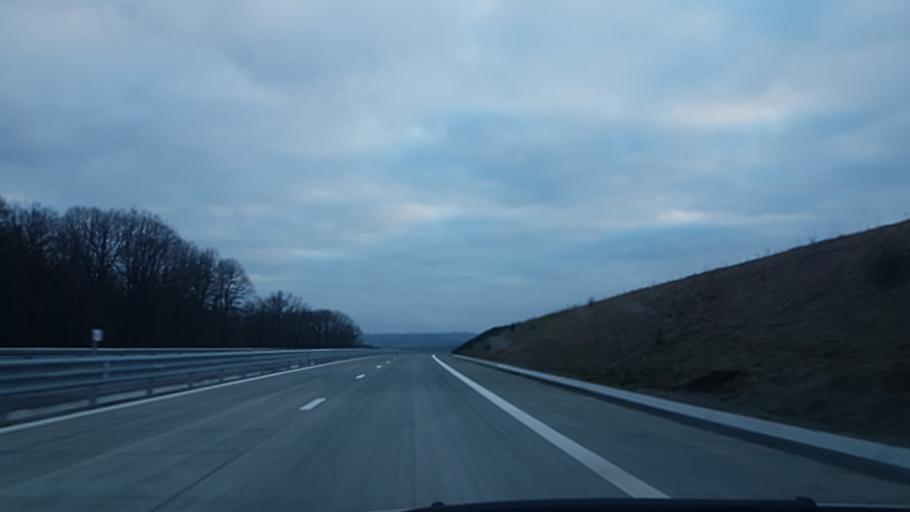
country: FR
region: Champagne-Ardenne
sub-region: Departement des Ardennes
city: Rocroi
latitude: 49.9920
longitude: 4.5423
